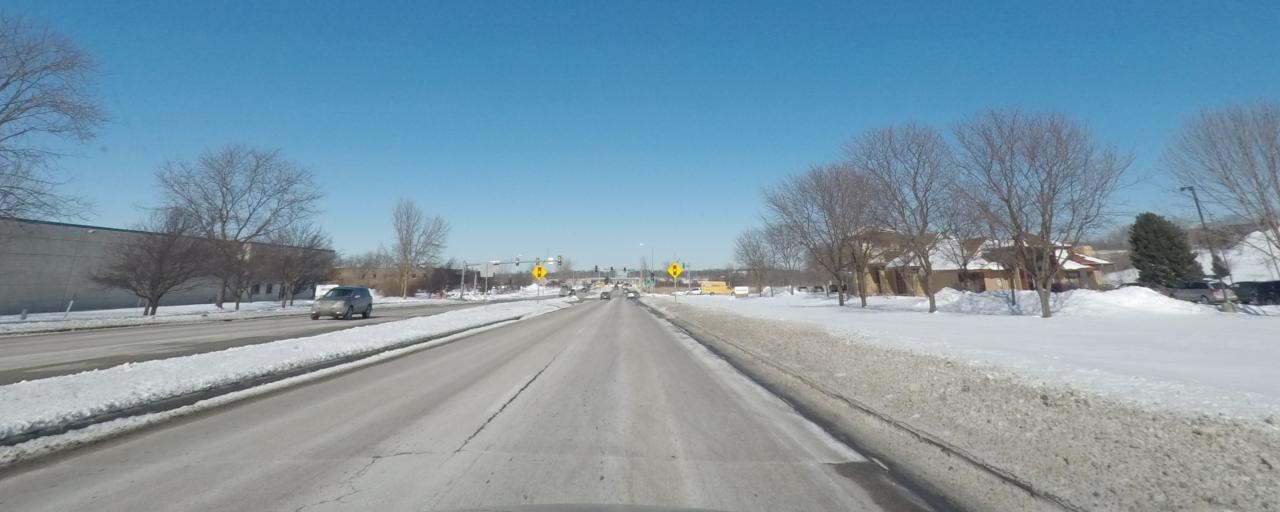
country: US
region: Wisconsin
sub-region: Waukesha County
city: New Berlin
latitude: 42.9454
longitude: -88.1091
